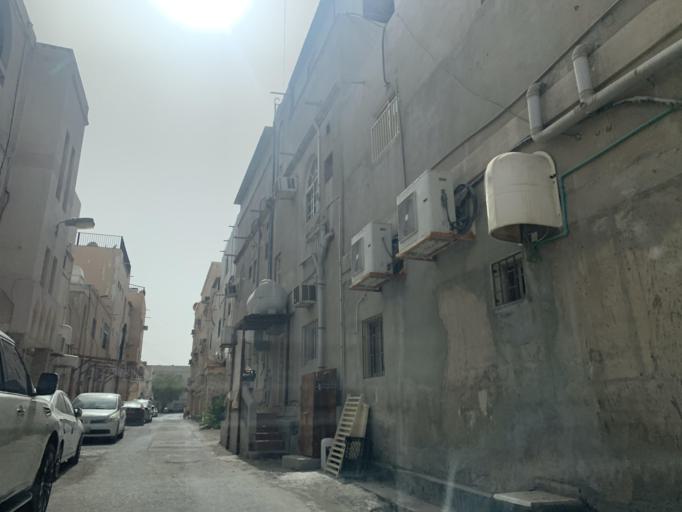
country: BH
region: Northern
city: Madinat `Isa
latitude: 26.1572
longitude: 50.5192
